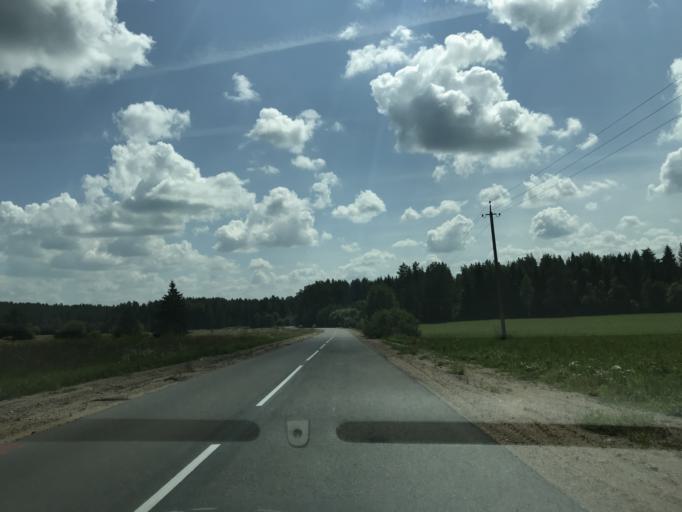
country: BY
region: Minsk
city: Rakaw
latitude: 54.0076
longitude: 26.9815
